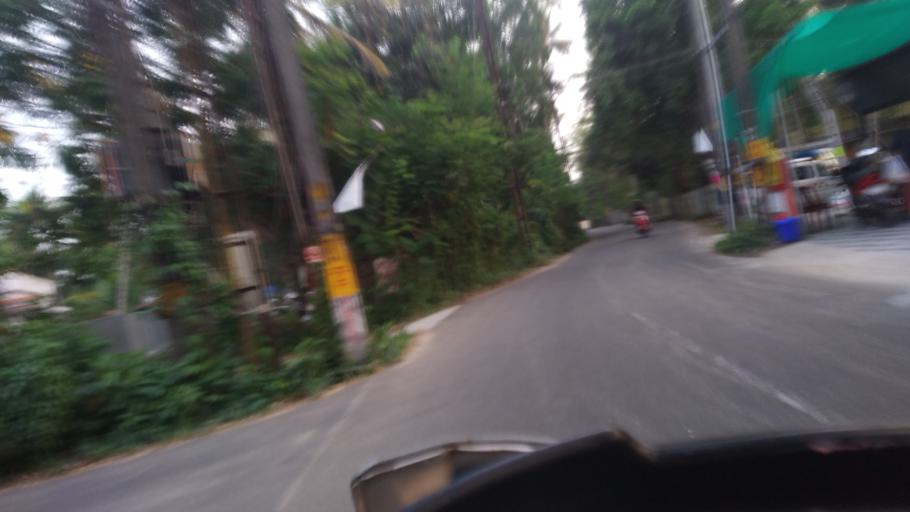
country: IN
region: Kerala
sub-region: Thrissur District
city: Kodungallur
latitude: 10.1728
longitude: 76.1987
